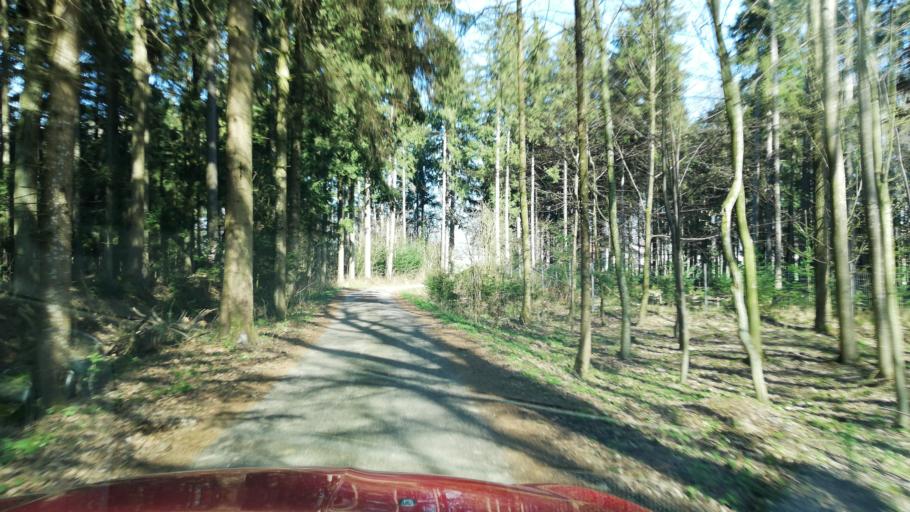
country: AT
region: Upper Austria
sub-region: Wels-Land
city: Sattledt
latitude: 48.0961
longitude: 14.0832
